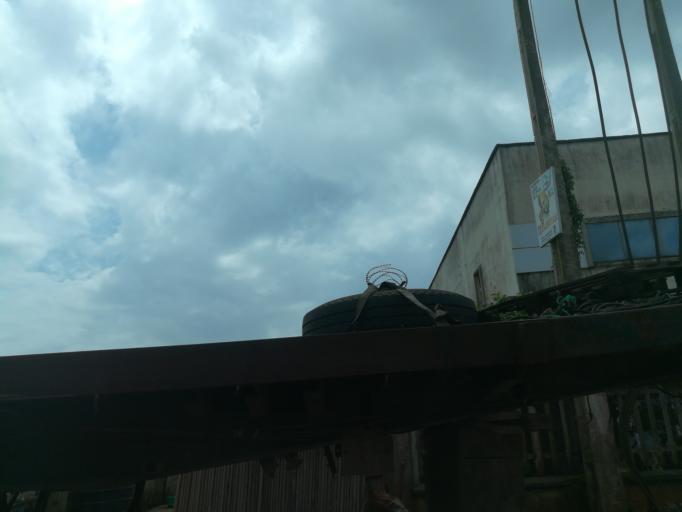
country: NG
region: Lagos
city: Ejirin
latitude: 6.6414
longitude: 3.7125
